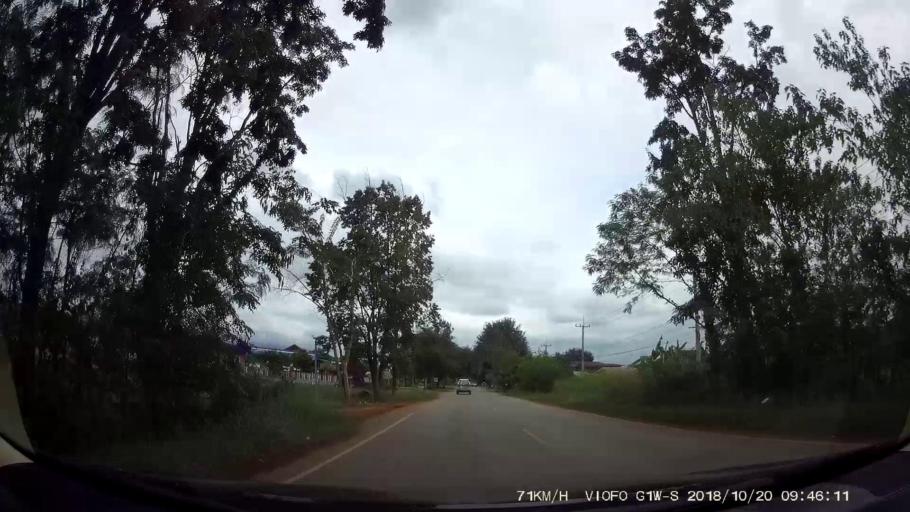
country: TH
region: Chaiyaphum
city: Khon San
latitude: 16.4943
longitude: 101.9287
